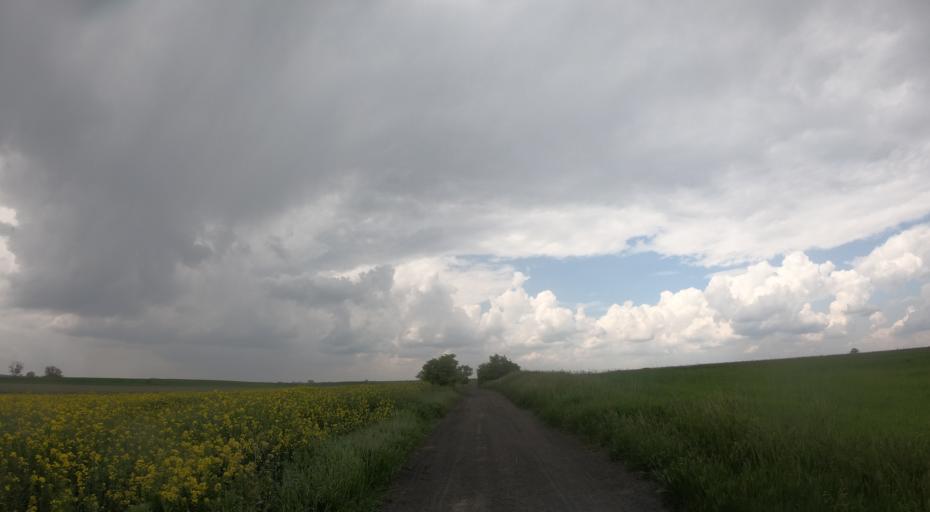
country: PL
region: West Pomeranian Voivodeship
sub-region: Powiat pyrzycki
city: Bielice
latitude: 53.2404
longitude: 14.7247
